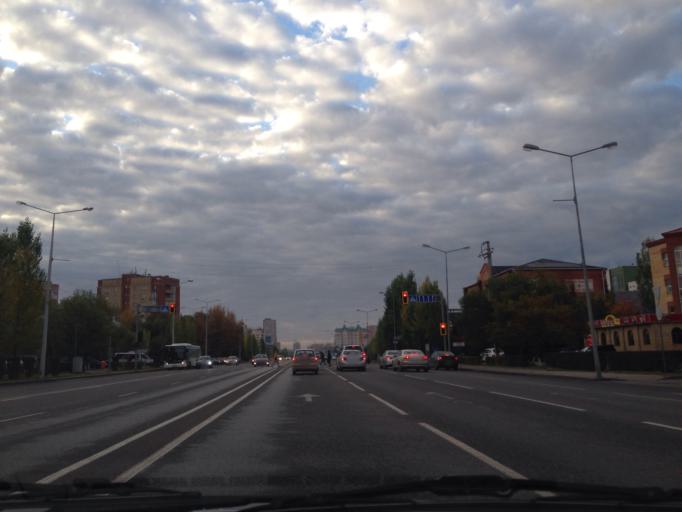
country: KZ
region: Astana Qalasy
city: Astana
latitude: 51.1495
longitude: 71.4575
